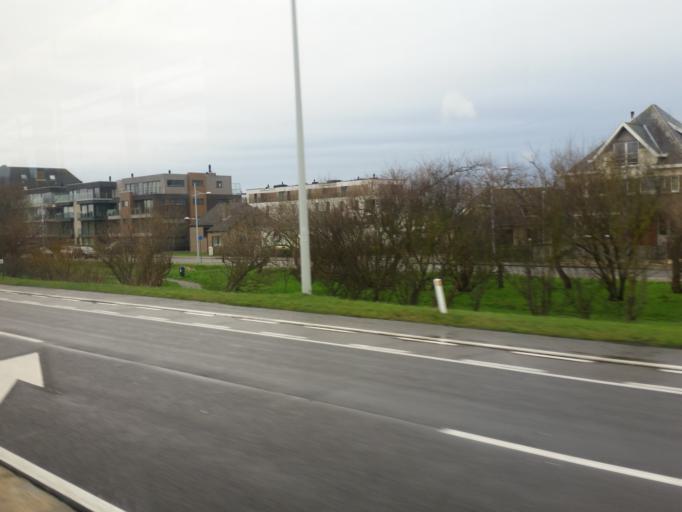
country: BE
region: Flanders
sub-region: Provincie West-Vlaanderen
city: Bredene
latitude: 51.2437
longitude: 2.9483
